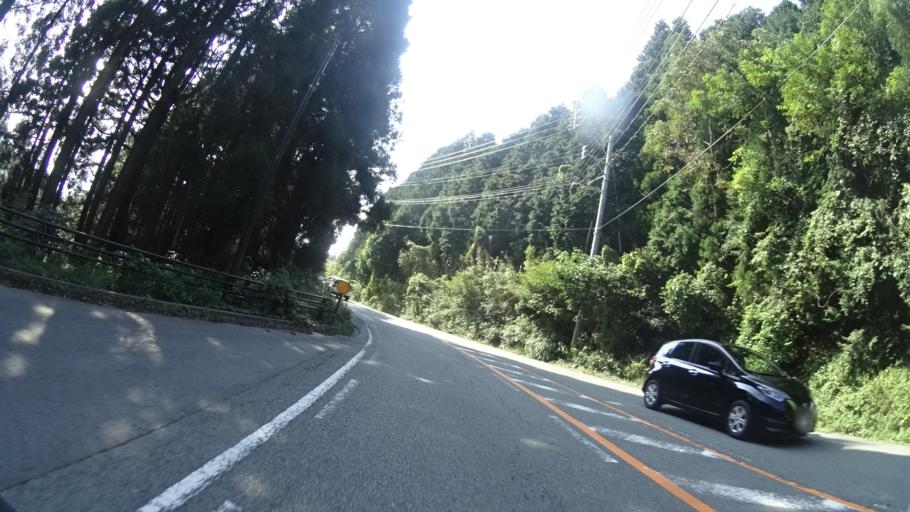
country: JP
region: Kumamoto
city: Ozu
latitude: 32.9082
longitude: 130.9501
